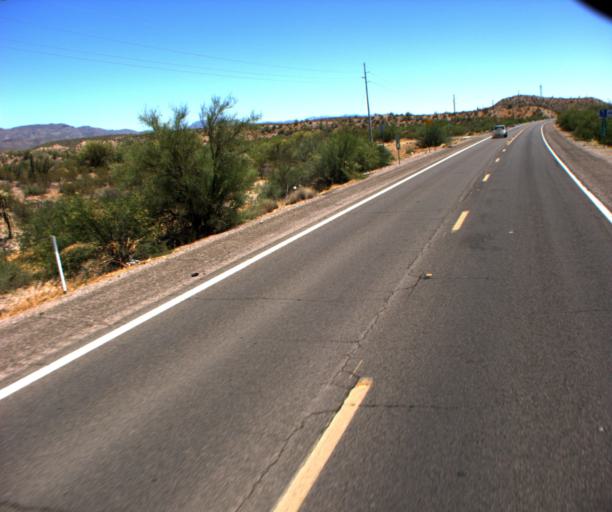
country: US
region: Arizona
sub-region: Pinal County
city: Kearny
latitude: 32.9545
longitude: -110.7460
